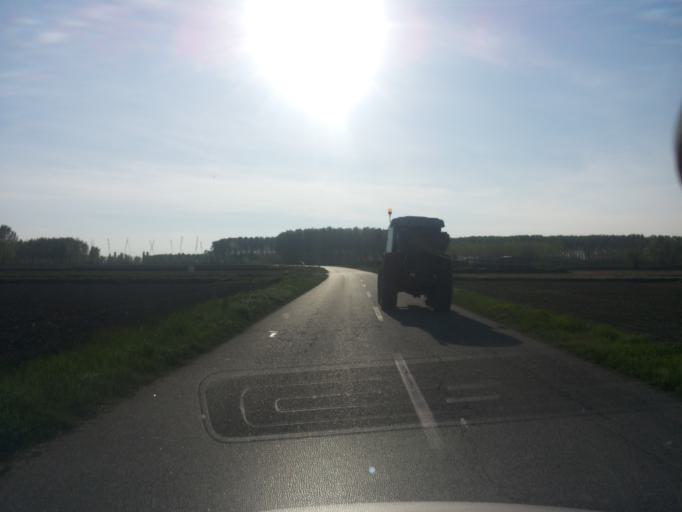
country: IT
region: Lombardy
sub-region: Provincia di Pavia
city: Cilavegna
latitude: 45.3045
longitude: 8.7281
